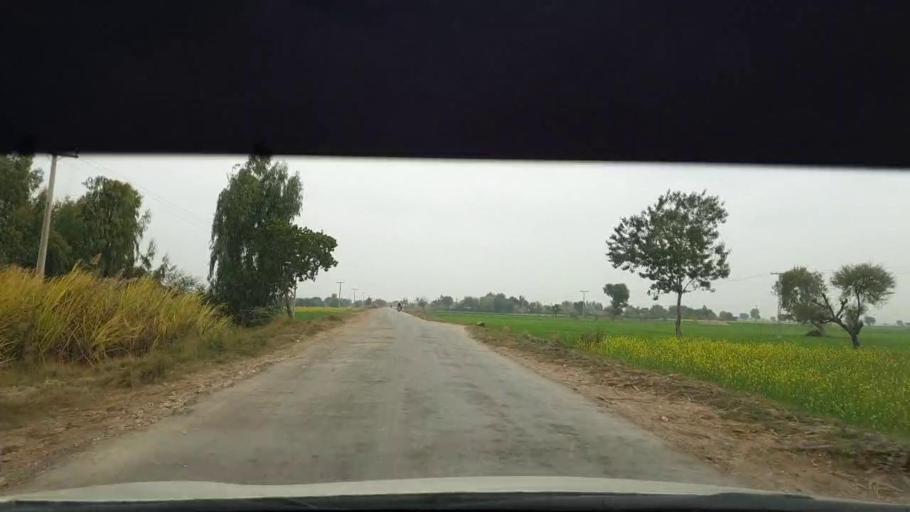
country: PK
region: Sindh
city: Berani
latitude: 25.7768
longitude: 68.8882
